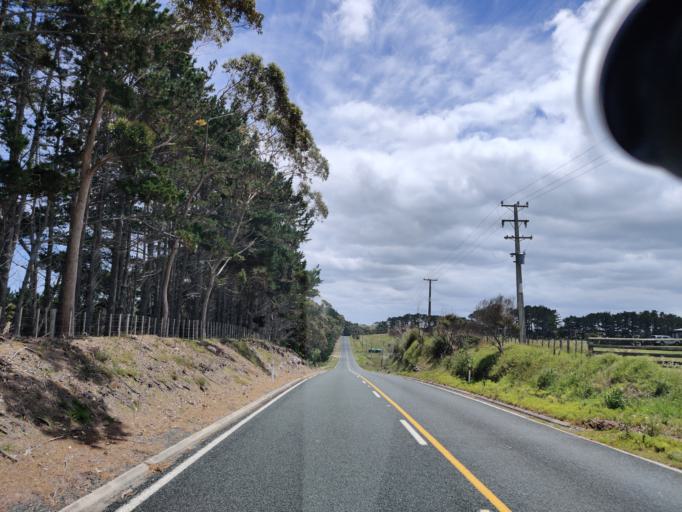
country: NZ
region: Northland
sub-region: Far North District
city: Kaitaia
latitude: -34.7155
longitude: 173.0386
